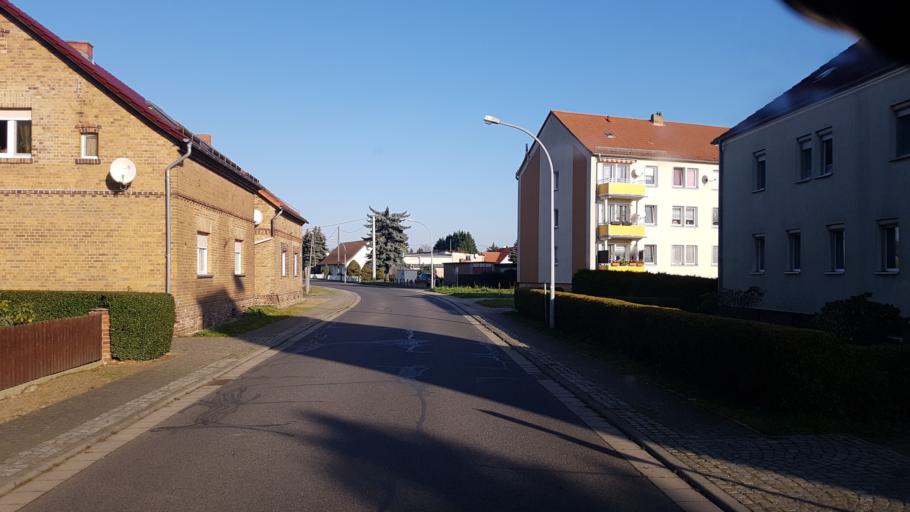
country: DE
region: Brandenburg
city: Schipkau
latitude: 51.5682
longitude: 13.9230
